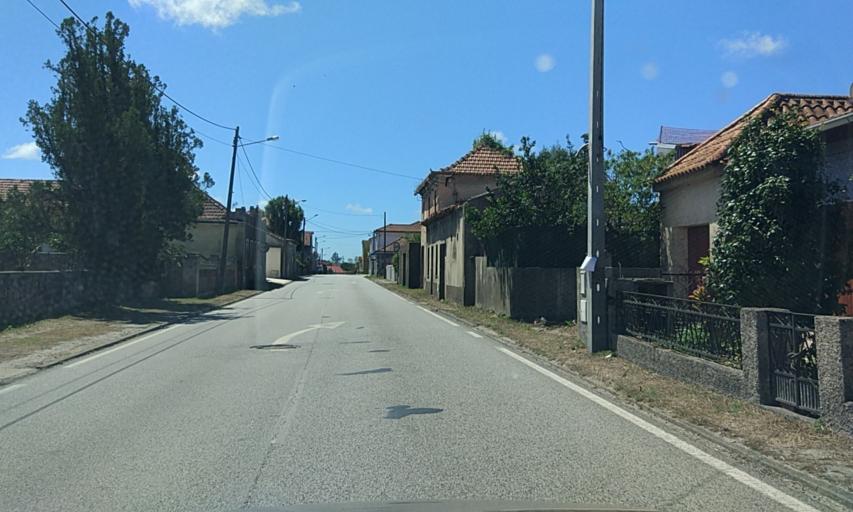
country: PT
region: Coimbra
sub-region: Mira
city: Mira
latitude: 40.4479
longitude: -8.7222
